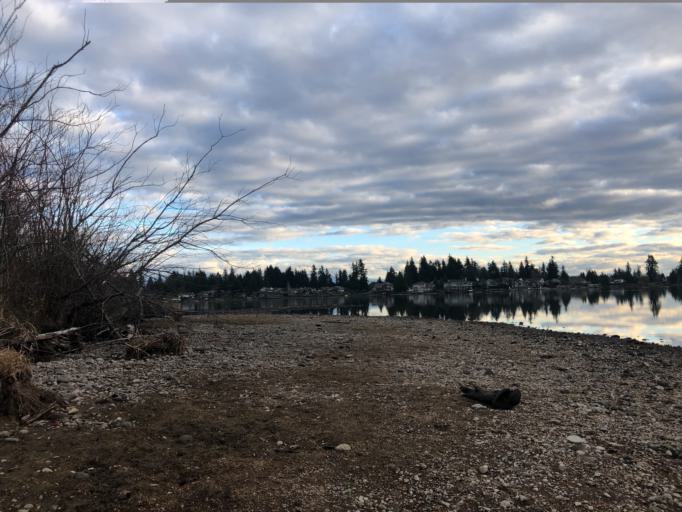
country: US
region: Washington
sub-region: Pierce County
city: Bonney Lake
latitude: 47.2372
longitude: -122.1614
